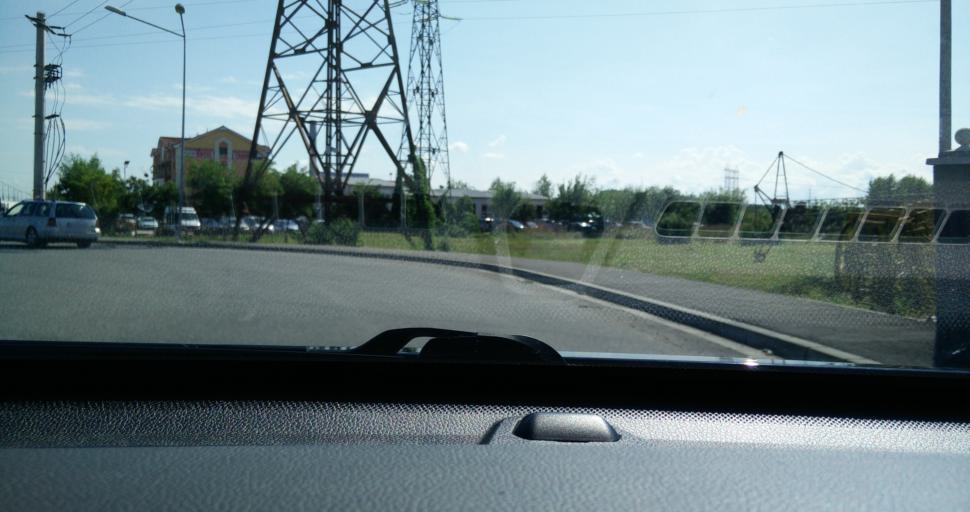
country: RO
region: Bihor
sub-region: Comuna Sanmartin
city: Sanmartin
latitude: 47.0275
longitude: 21.9661
